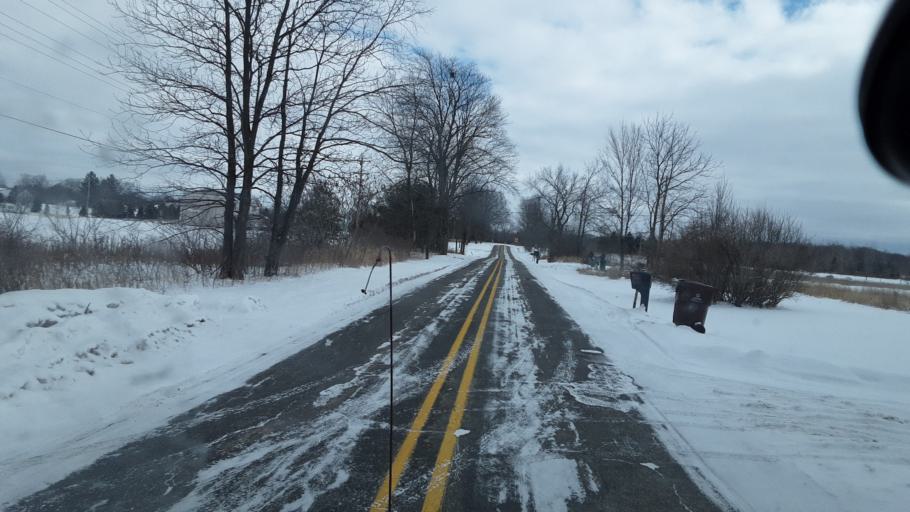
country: US
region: Michigan
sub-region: Ingham County
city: Holt
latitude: 42.6149
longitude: -84.5480
